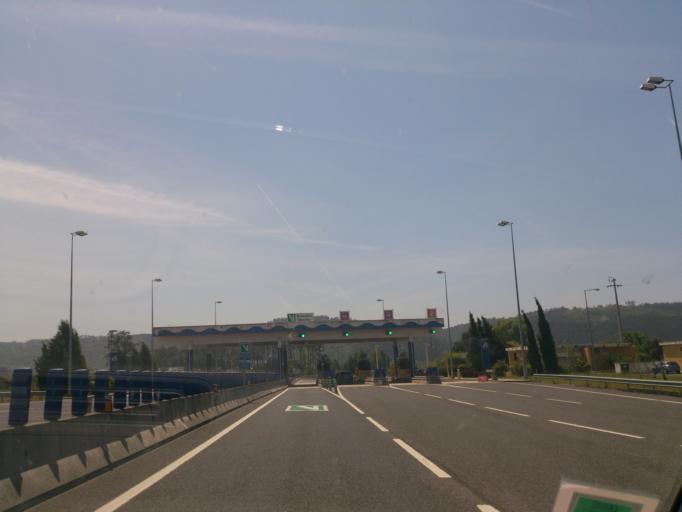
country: PT
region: Leiria
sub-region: Alcobaca
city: Alcobaca
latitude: 39.5851
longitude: -9.0088
